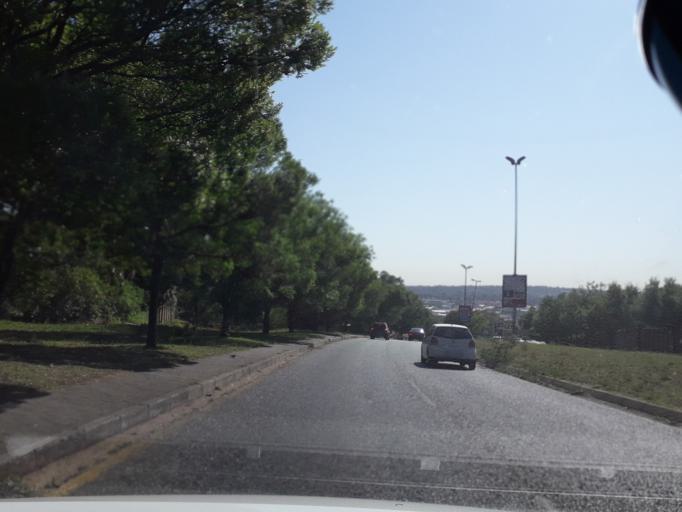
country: ZA
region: Gauteng
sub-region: City of Johannesburg Metropolitan Municipality
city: Roodepoort
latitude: -26.0929
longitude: 27.9564
